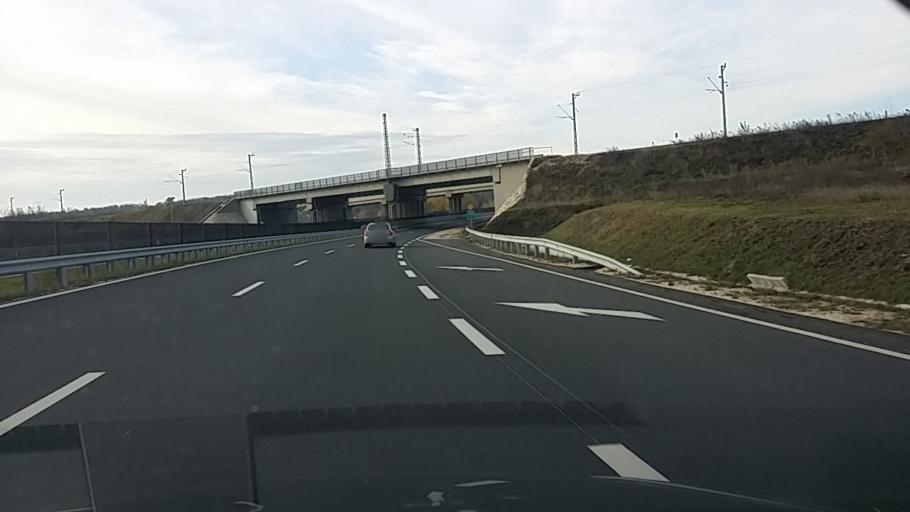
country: HU
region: Veszprem
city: Varpalota
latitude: 47.1842
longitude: 18.1351
